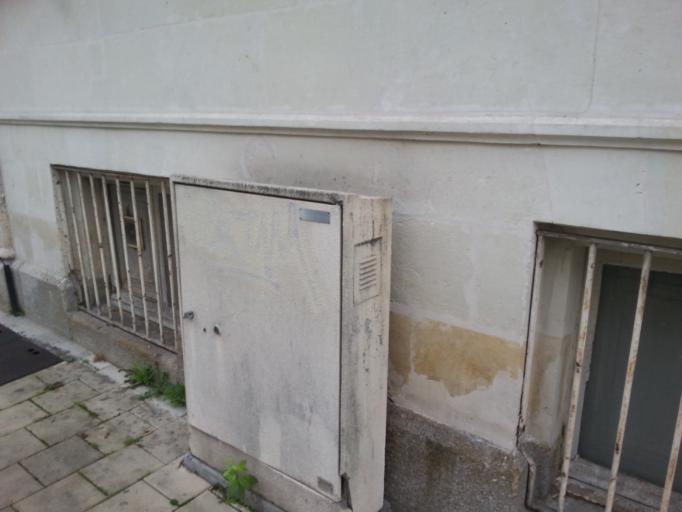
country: FR
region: Pays de la Loire
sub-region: Departement de Maine-et-Loire
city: Angers
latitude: 47.4667
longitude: -0.5545
